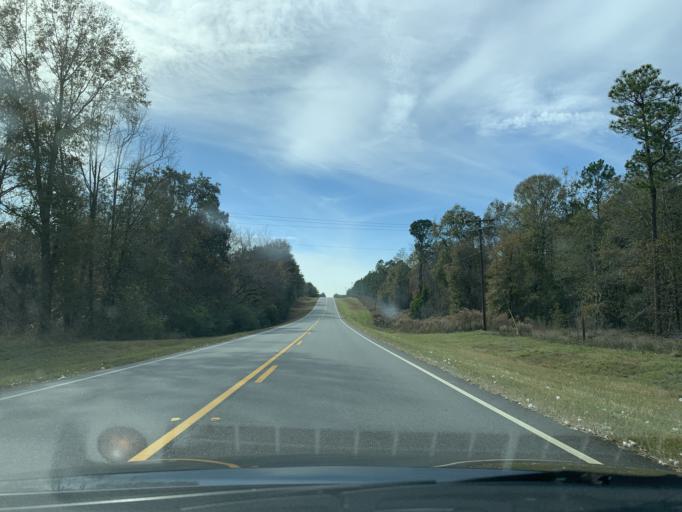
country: US
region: Georgia
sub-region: Turner County
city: Ashburn
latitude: 31.7587
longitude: -83.5473
